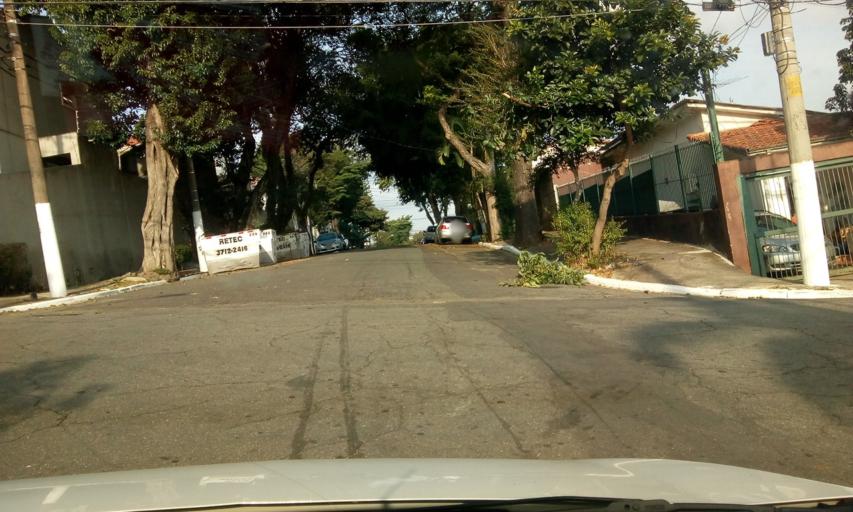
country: BR
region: Sao Paulo
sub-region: Sao Paulo
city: Sao Paulo
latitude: -23.6184
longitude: -46.6552
